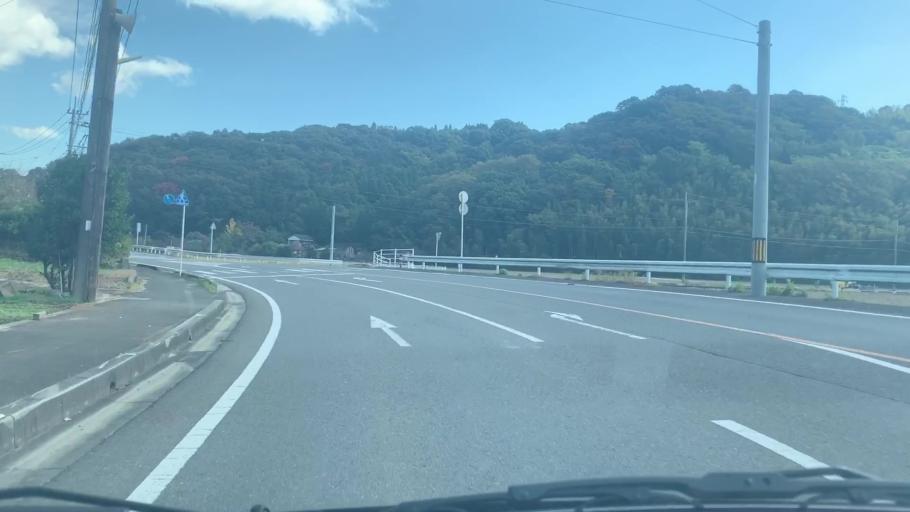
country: JP
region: Saga Prefecture
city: Saga-shi
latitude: 33.2668
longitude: 130.1775
